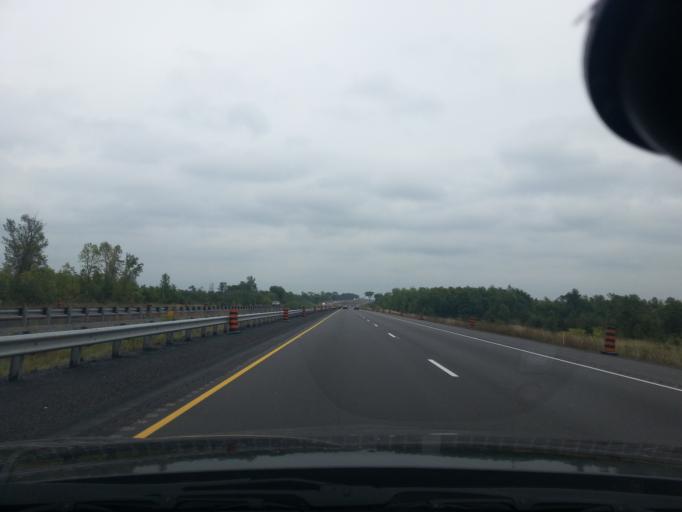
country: CA
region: Ontario
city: Skatepark
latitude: 44.2750
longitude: -76.8742
